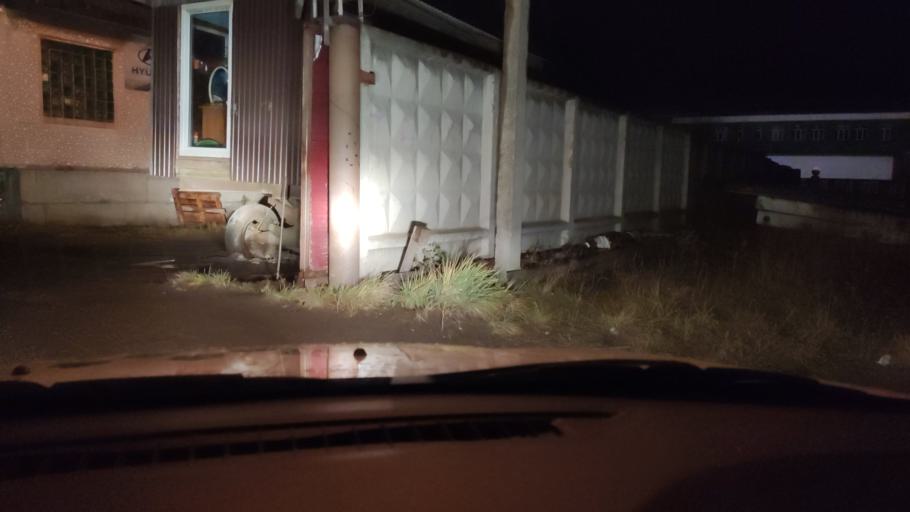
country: RU
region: Perm
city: Kondratovo
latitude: 58.0072
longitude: 56.1500
